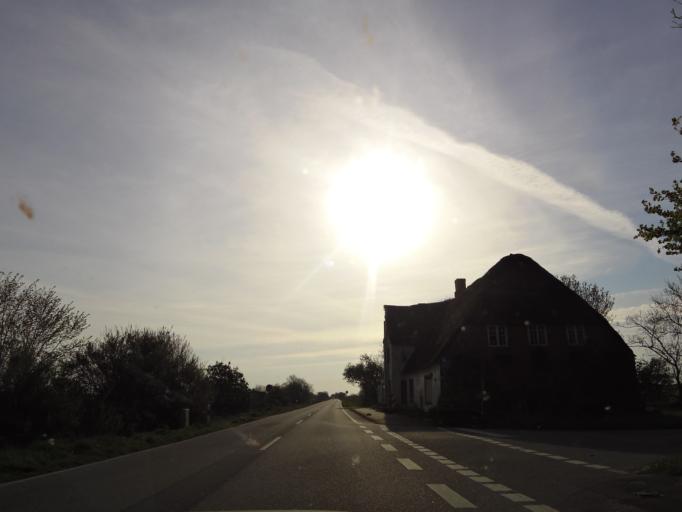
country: DE
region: Schleswig-Holstein
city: Galmsbull
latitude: 54.7749
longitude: 8.7722
